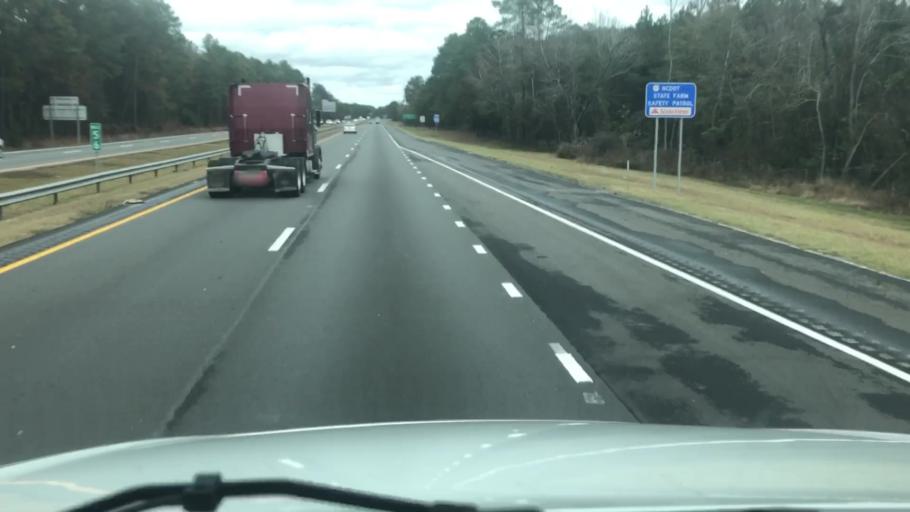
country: US
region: North Carolina
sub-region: Cumberland County
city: Eastover
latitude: 35.1011
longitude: -78.7736
